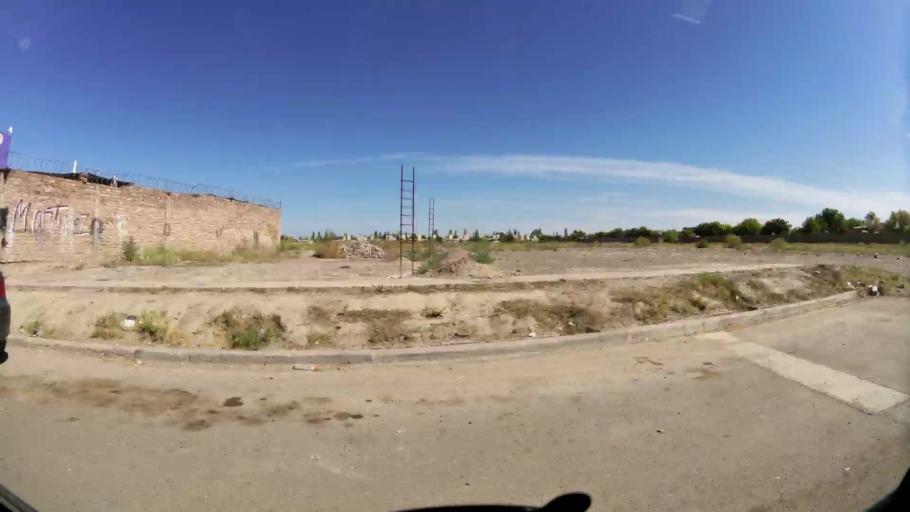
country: AR
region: Mendoza
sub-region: Departamento de Godoy Cruz
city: Godoy Cruz
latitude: -32.9560
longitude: -68.8269
